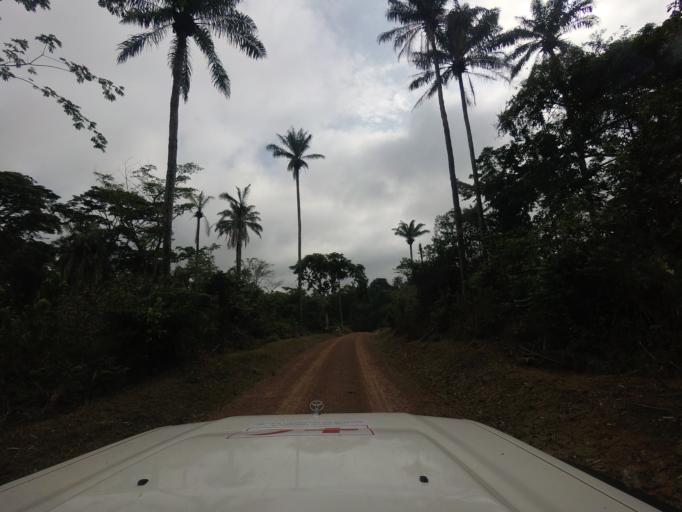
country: LR
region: Lofa
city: Voinjama
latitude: 8.4586
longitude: -9.7931
